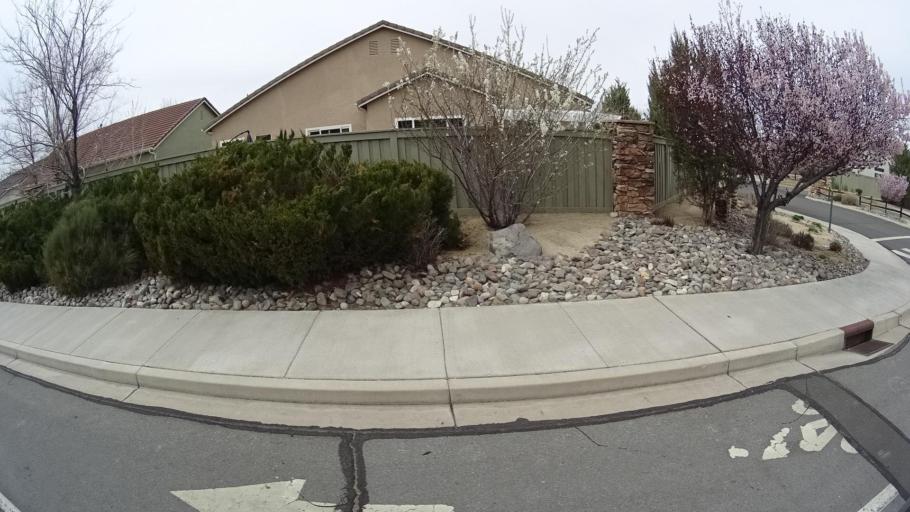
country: US
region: Nevada
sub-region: Washoe County
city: Sparks
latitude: 39.4407
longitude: -119.7358
